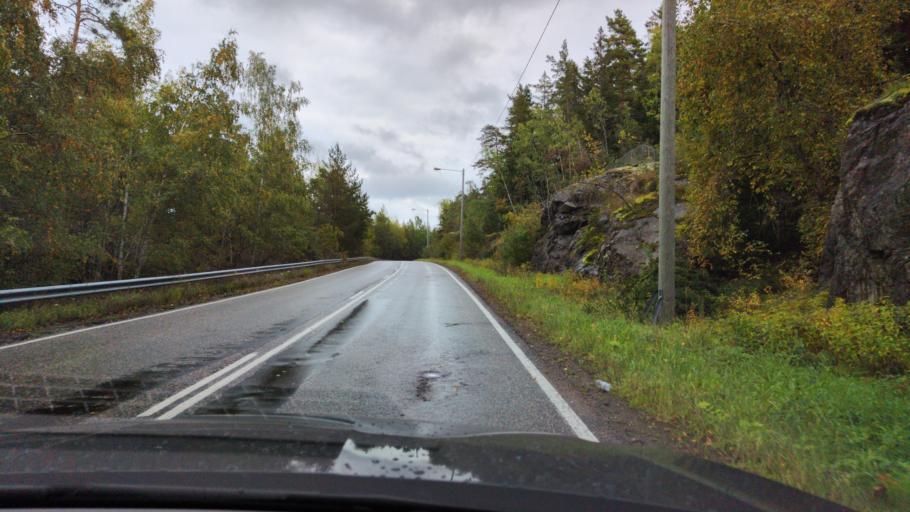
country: FI
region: Varsinais-Suomi
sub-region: Turku
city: Turku
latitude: 60.3670
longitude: 22.2137
